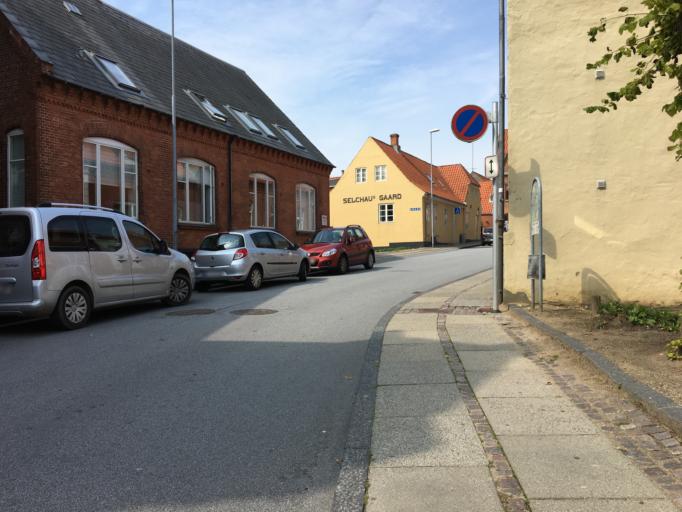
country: DK
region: Central Jutland
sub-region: Skive Kommune
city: Skive
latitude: 56.5687
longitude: 9.0286
